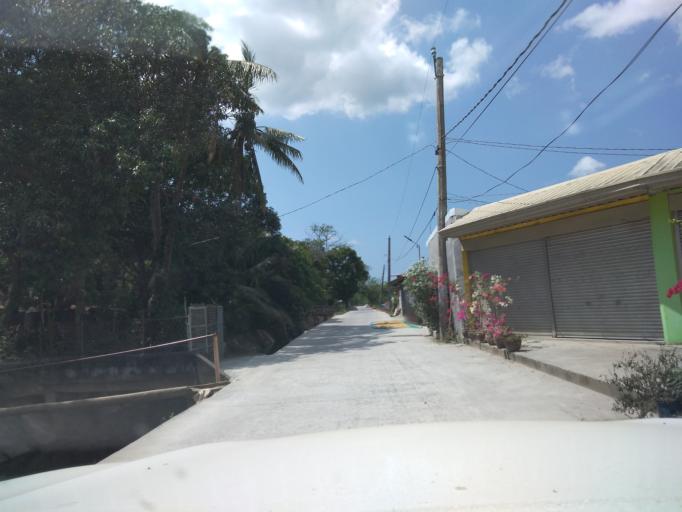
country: PH
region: Central Luzon
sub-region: Province of Pampanga
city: Bahay Pare
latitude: 15.0335
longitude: 120.8767
